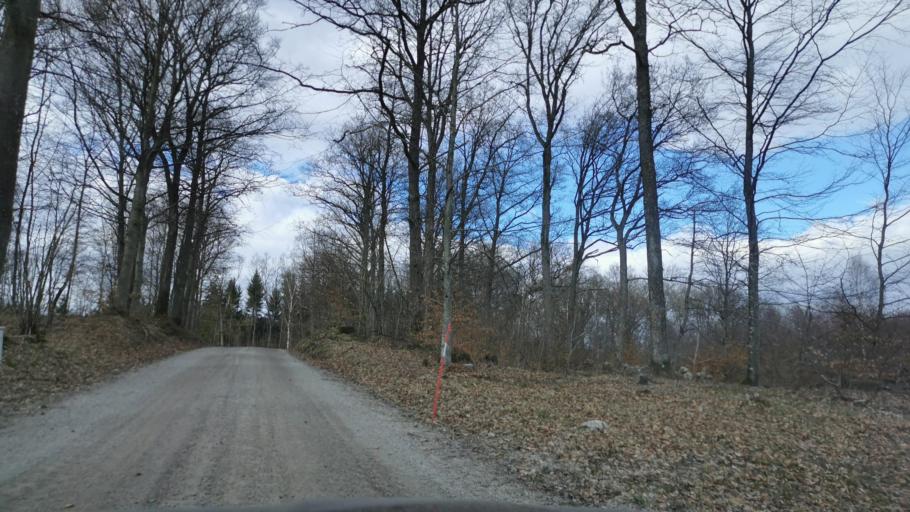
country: SE
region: Skane
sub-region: Sjobo Kommun
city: Sjoebo
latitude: 55.7447
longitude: 13.8381
